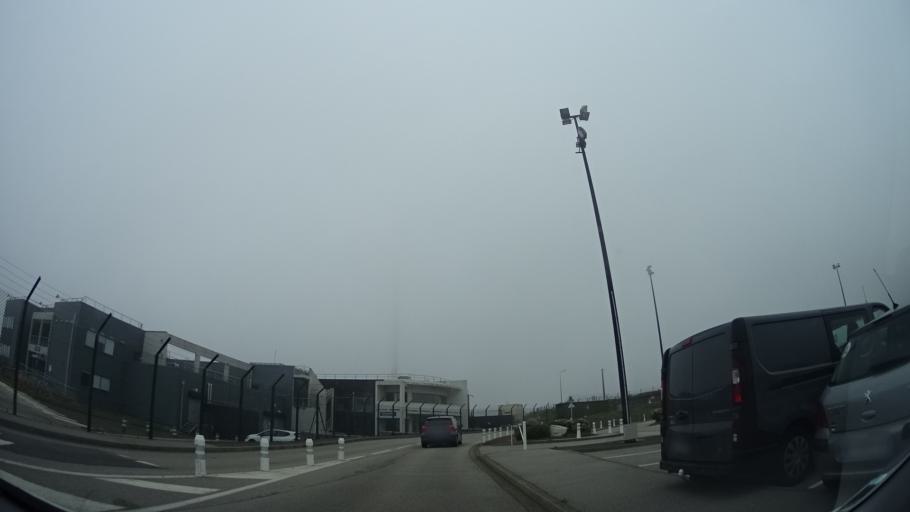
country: FR
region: Lower Normandy
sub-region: Departement de la Manche
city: Flamanville
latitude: 49.5315
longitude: -1.8811
